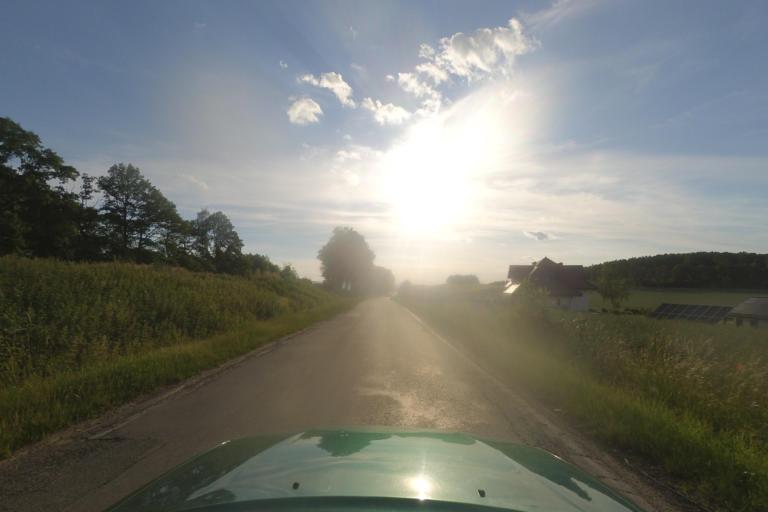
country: PL
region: Lower Silesian Voivodeship
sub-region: Powiat dzierzoniowski
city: Pilawa Gorna
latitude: 50.7292
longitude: 16.7360
